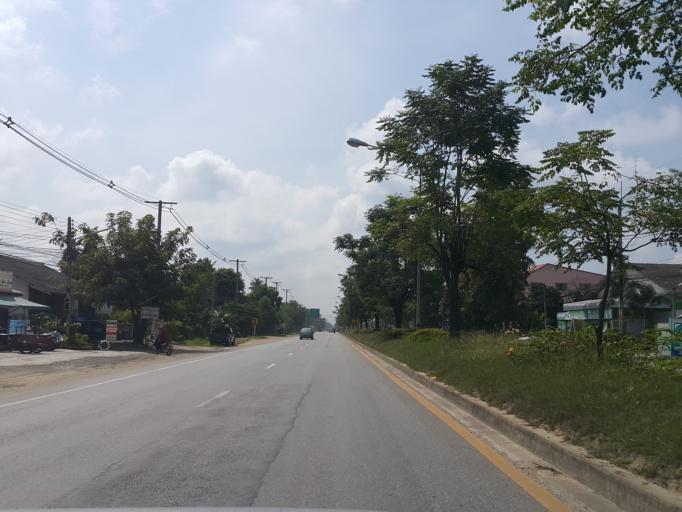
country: TH
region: Chiang Mai
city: San Sai
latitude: 18.9253
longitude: 98.9927
